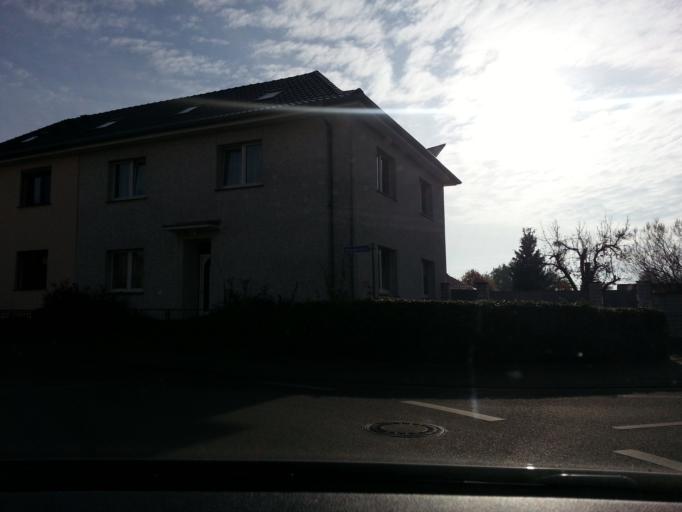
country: DE
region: Mecklenburg-Vorpommern
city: Torgelow
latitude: 53.6328
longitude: 14.0158
